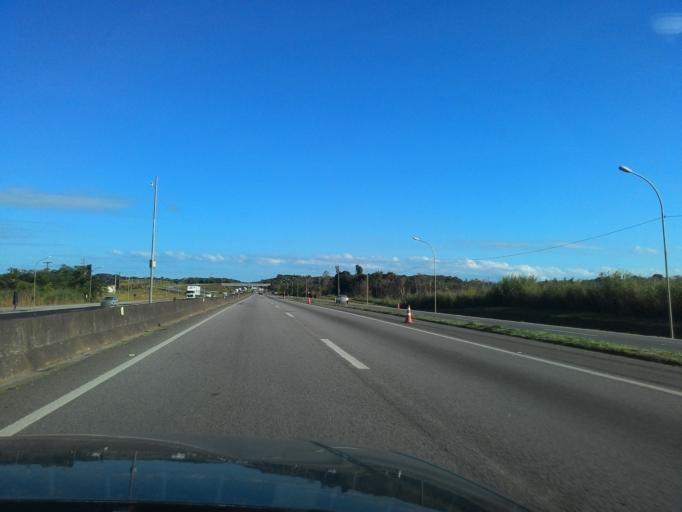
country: BR
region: Sao Paulo
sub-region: Registro
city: Registro
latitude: -24.5332
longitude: -47.8578
